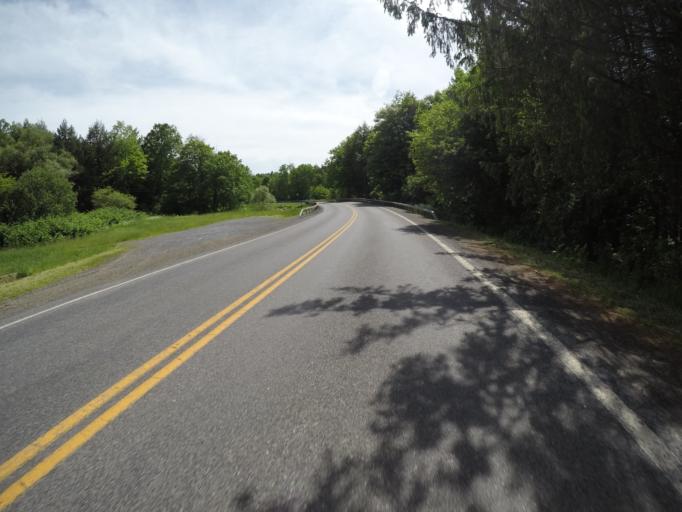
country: US
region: New York
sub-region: Delaware County
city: Delhi
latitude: 42.1203
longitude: -74.8201
